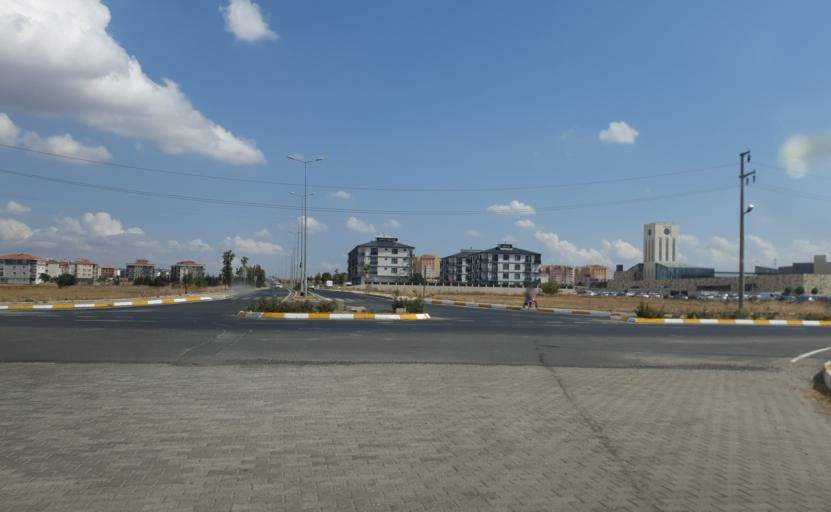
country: TR
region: Kirklareli
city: Luleburgaz
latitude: 41.3875
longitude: 27.3476
